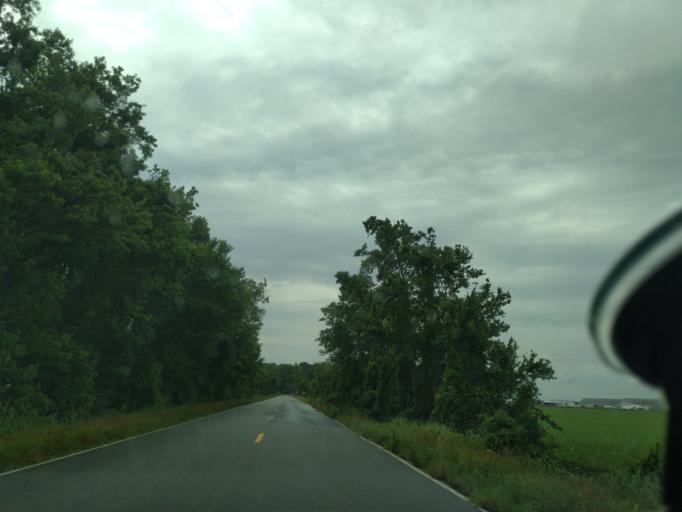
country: US
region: North Carolina
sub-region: Washington County
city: Plymouth
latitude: 35.8294
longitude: -76.5184
